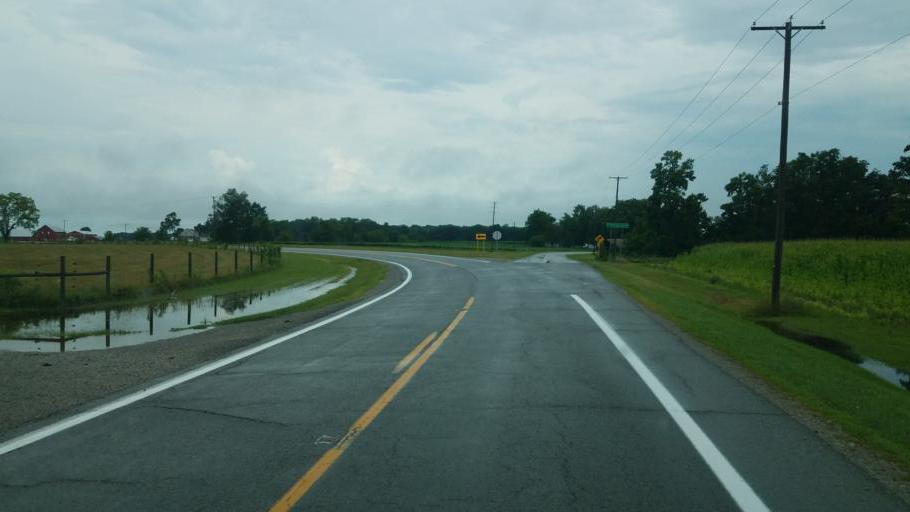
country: US
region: Ohio
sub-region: Marion County
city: Prospect
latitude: 40.5128
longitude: -83.2573
